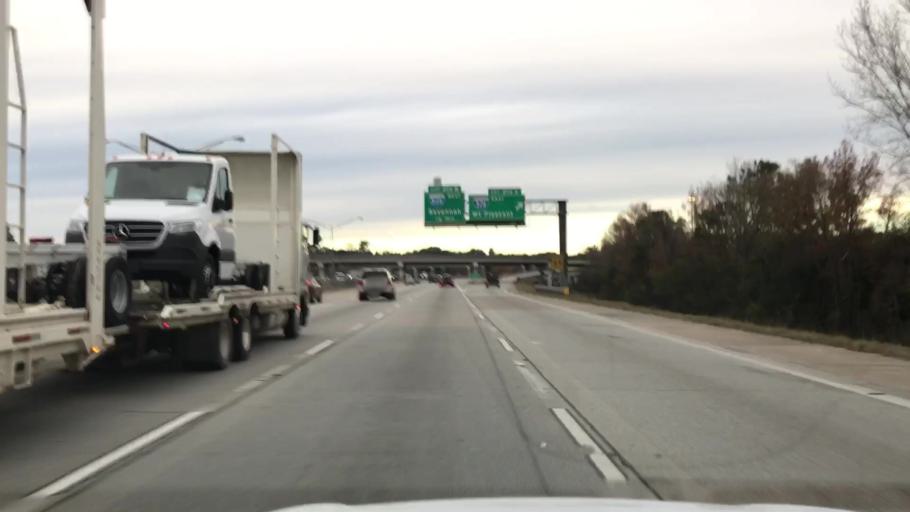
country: US
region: South Carolina
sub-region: Berkeley County
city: Hanahan
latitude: 32.8798
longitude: -80.0174
